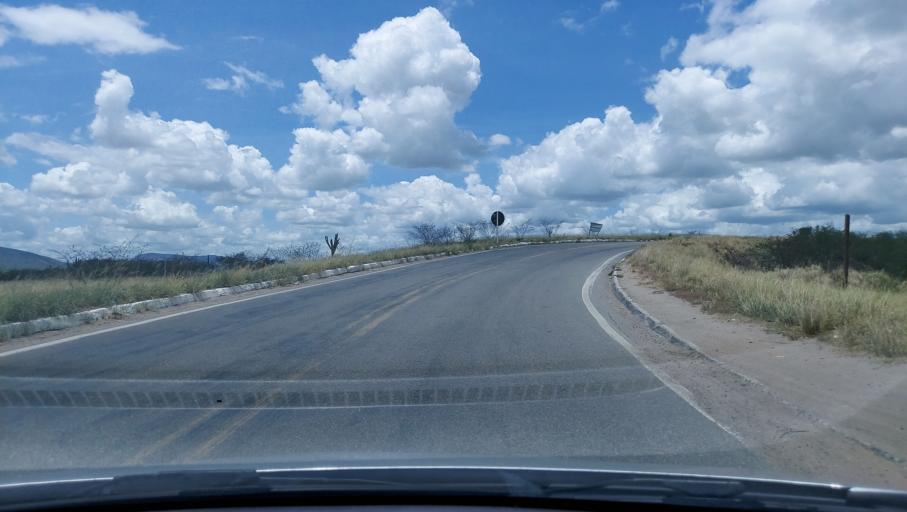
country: BR
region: Bahia
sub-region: Castro Alves
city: Castro Alves
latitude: -12.5831
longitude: -39.5211
